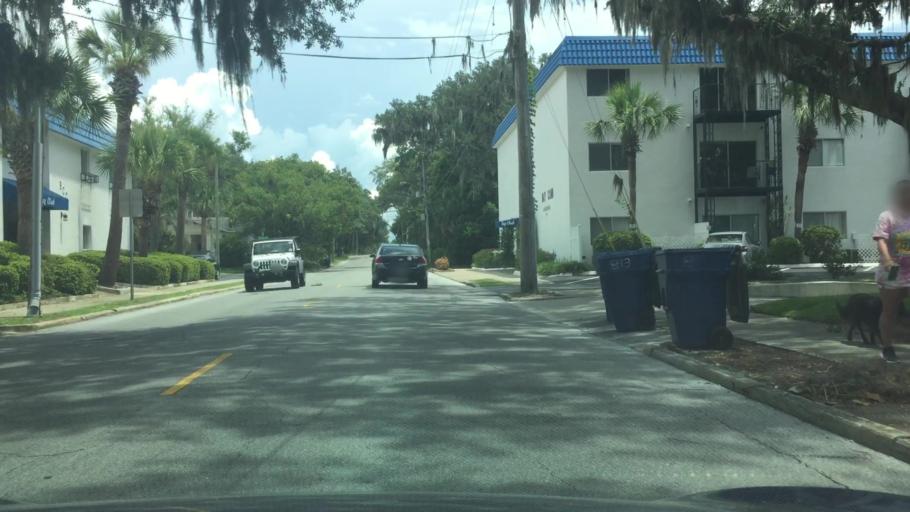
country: US
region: Florida
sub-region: Bay County
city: Panama City
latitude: 30.1459
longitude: -85.6554
